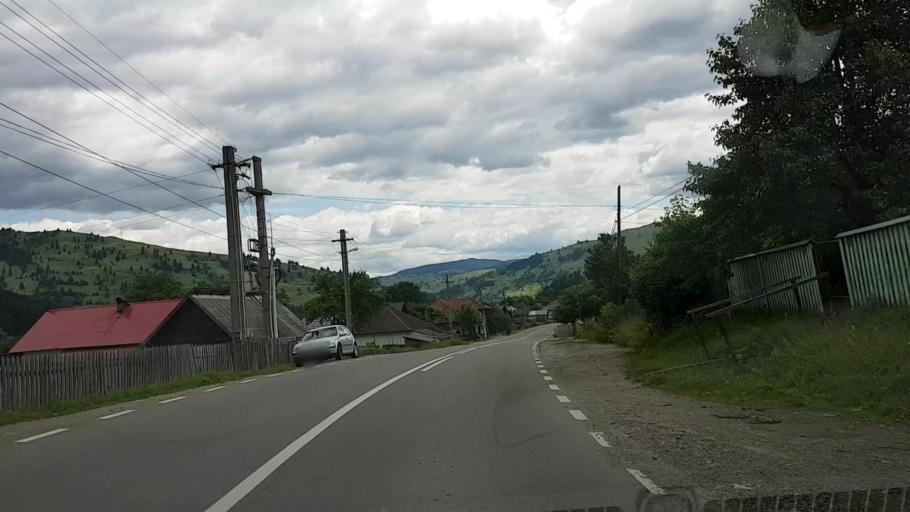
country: RO
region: Neamt
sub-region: Comuna Borca
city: Borca
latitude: 47.1906
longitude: 25.7713
